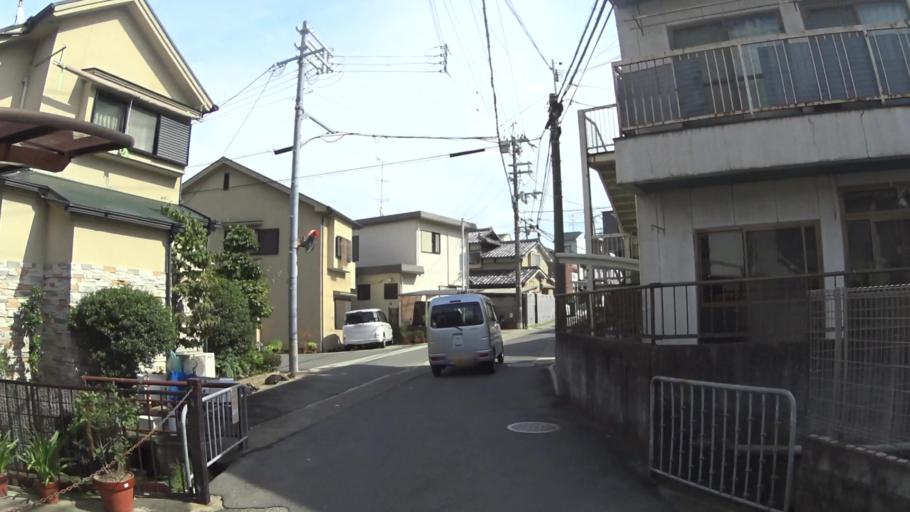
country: JP
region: Kyoto
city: Muko
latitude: 34.9831
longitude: 135.6882
